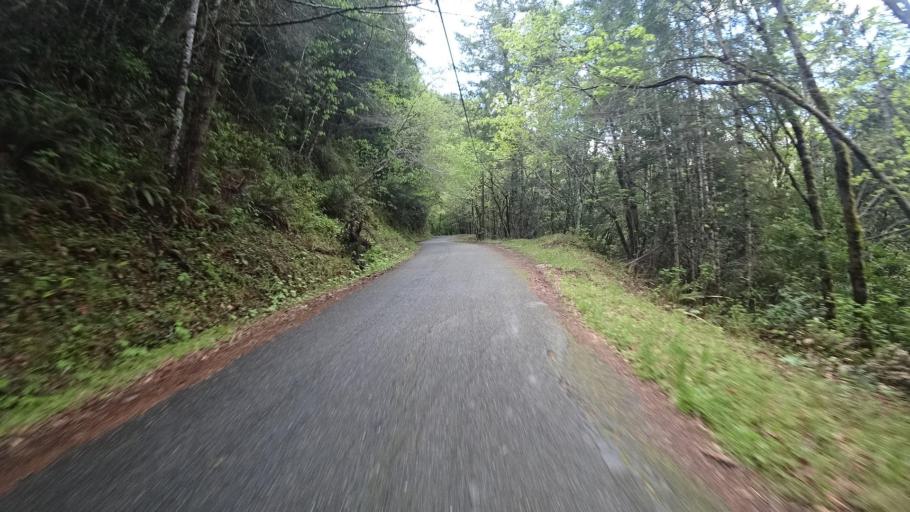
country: US
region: California
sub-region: Humboldt County
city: Blue Lake
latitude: 40.7605
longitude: -123.9052
